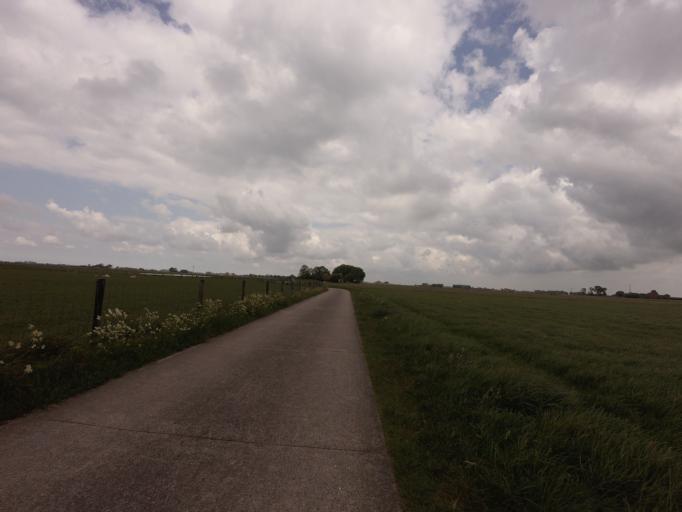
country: NL
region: Friesland
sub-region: Gemeente Littenseradiel
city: Wommels
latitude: 53.1099
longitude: 5.5996
